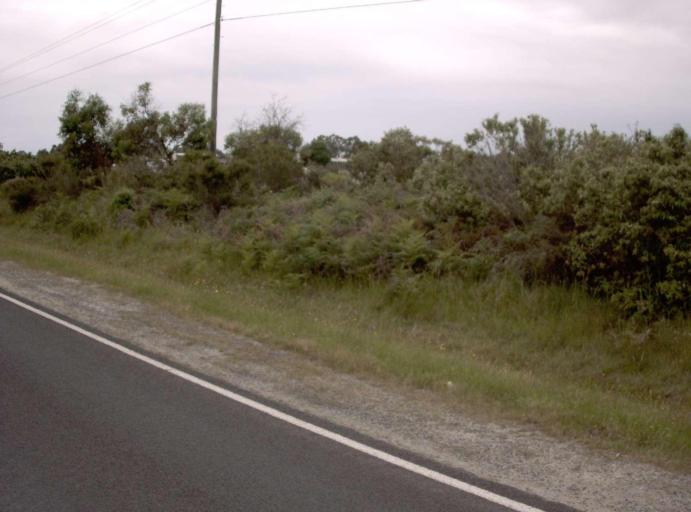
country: AU
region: Victoria
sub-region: Baw Baw
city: Warragul
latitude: -38.5803
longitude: 146.0455
